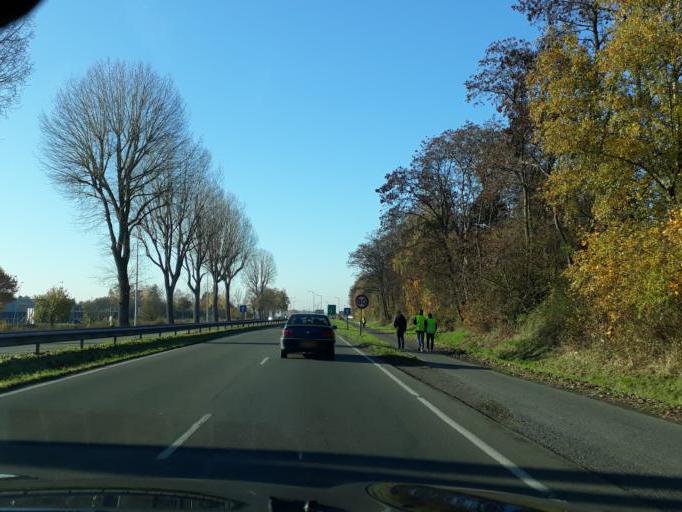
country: FR
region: Nord-Pas-de-Calais
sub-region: Departement du Nord
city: Dechy
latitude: 50.3438
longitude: 3.1072
